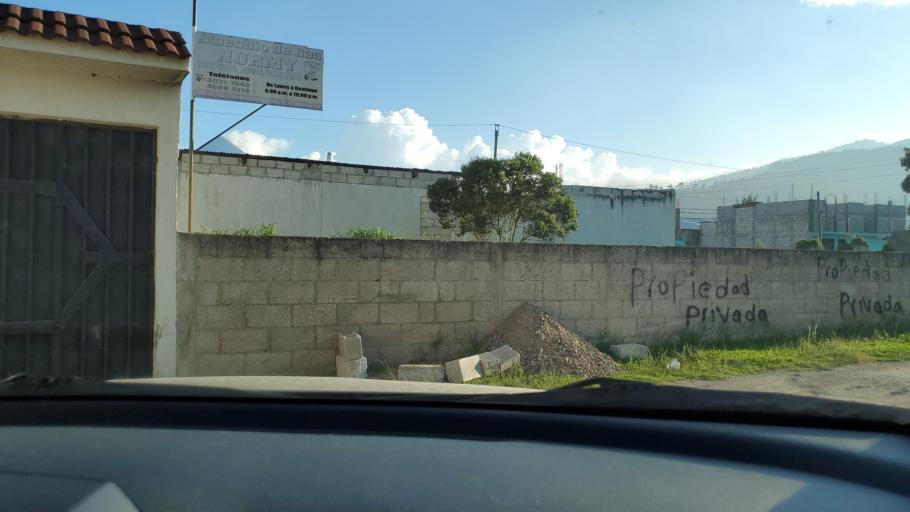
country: GT
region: Quetzaltenango
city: Quetzaltenango
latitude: 14.8349
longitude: -91.5458
